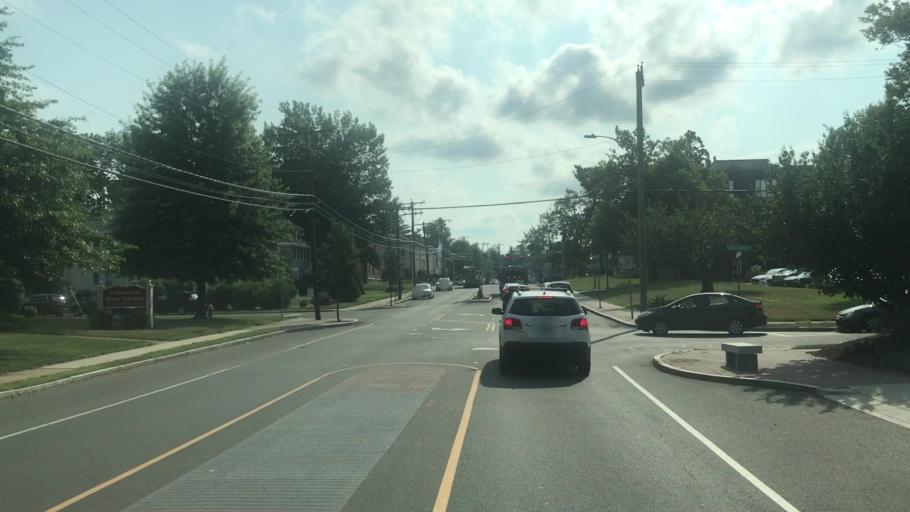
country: US
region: Connecticut
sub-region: Hartford County
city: West Hartford
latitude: 41.7643
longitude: -72.7310
